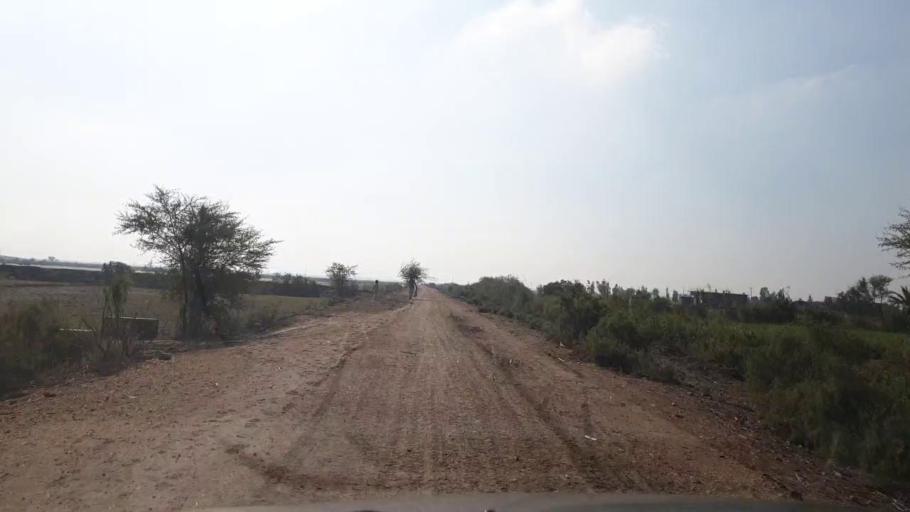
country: PK
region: Sindh
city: Sinjhoro
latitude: 26.0406
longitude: 68.7785
